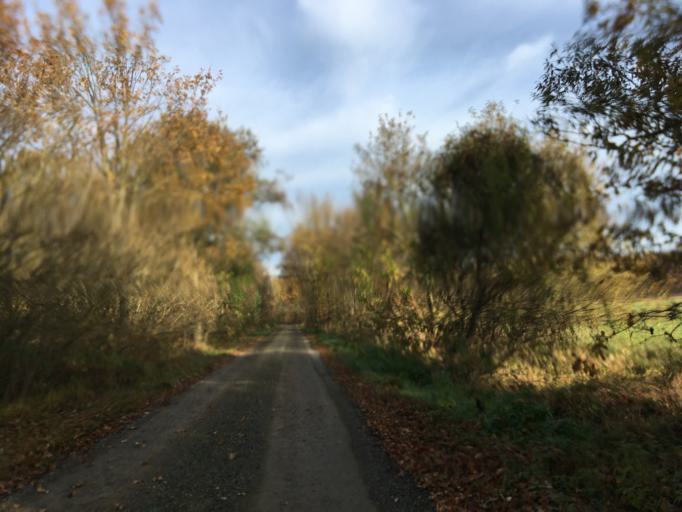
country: DE
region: Brandenburg
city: Luebben
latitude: 51.9860
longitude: 13.8727
